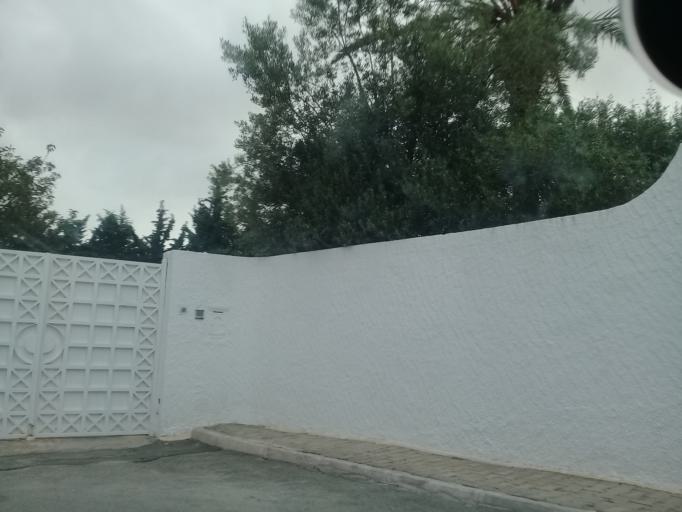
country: TN
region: Tunis
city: Sidi Bou Said
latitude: 36.8734
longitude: 10.3412
